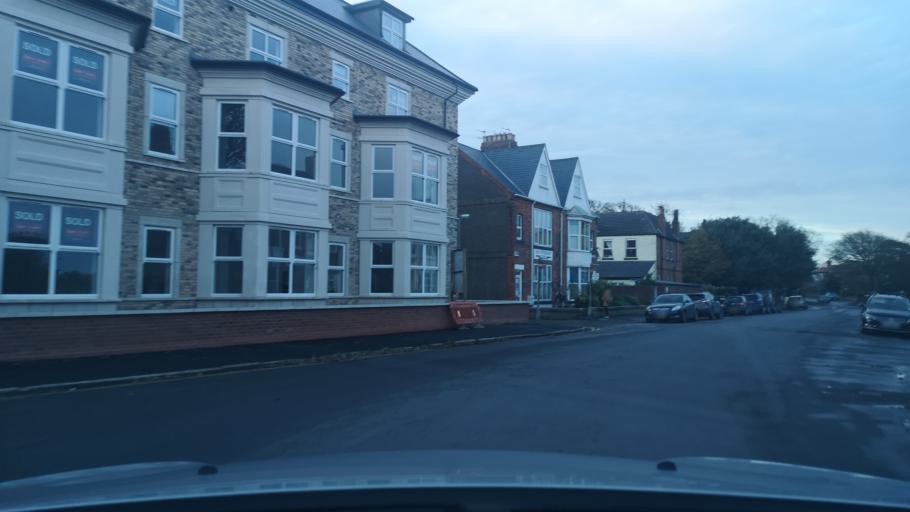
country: GB
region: England
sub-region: East Riding of Yorkshire
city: Hornsea
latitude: 53.9117
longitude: -0.1635
